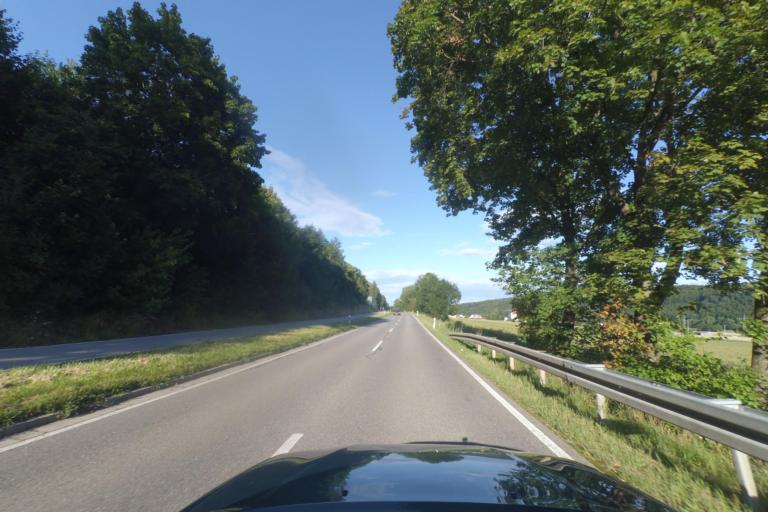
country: DE
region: Bavaria
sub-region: Upper Bavaria
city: Eichstaett
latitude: 48.8811
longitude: 11.2269
